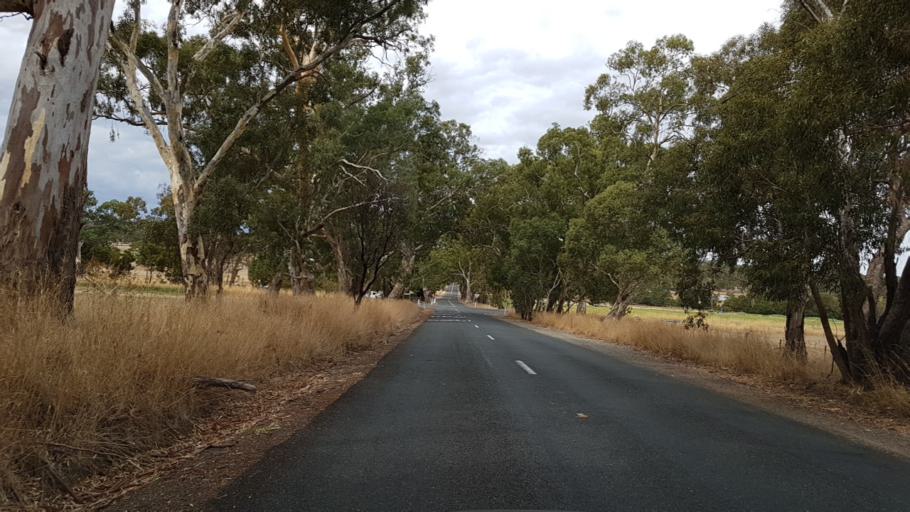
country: AU
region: South Australia
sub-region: Adelaide Hills
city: Birdwood
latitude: -34.7906
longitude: 138.9534
